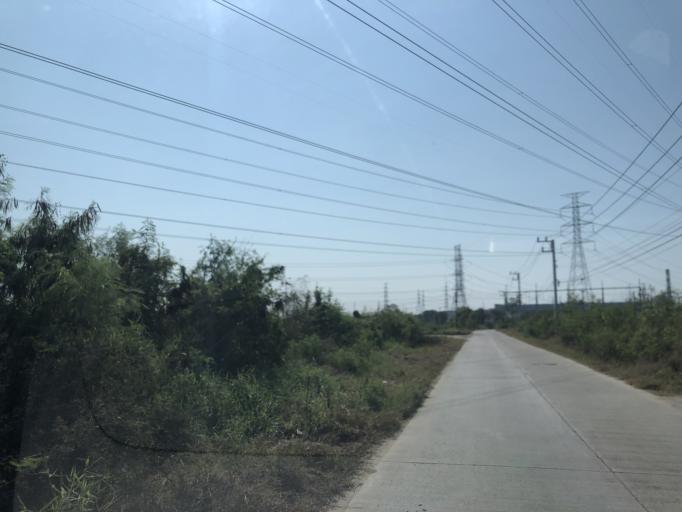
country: TH
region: Chachoengsao
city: Bang Pakong
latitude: 13.5142
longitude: 101.0241
